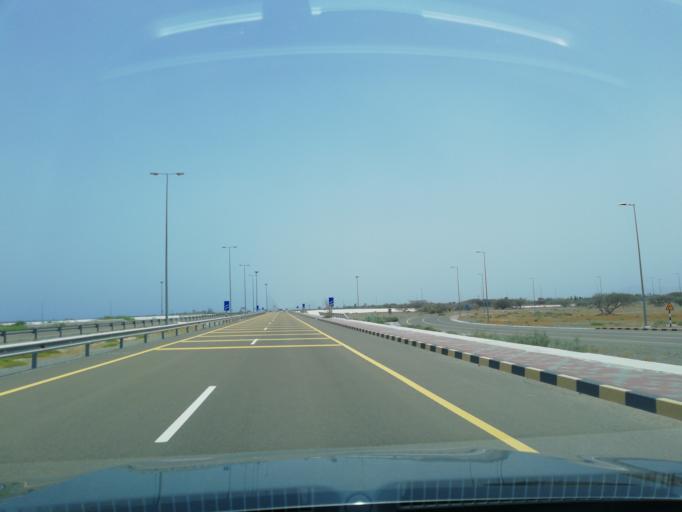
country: OM
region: Al Batinah
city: Shinas
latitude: 24.9203
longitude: 56.3872
